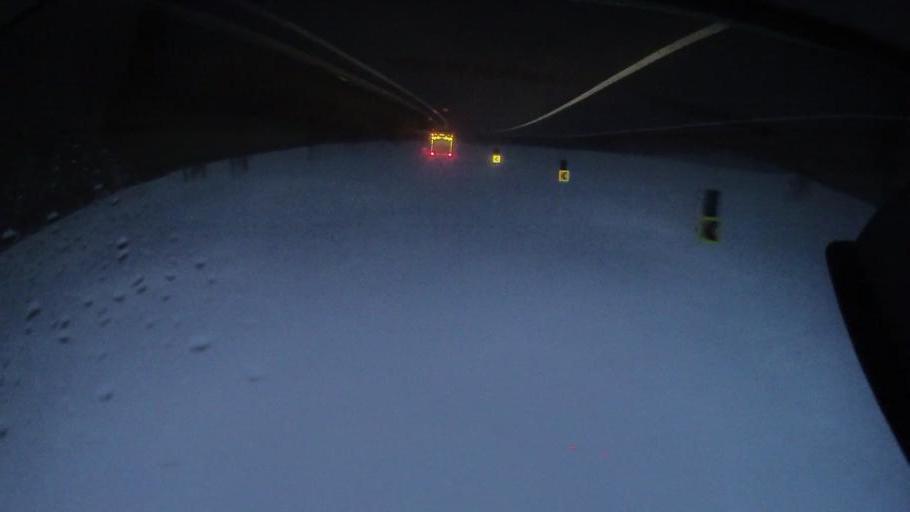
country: RO
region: Harghita
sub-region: Comuna Subcetate
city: Subcetate
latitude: 46.8464
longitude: 25.4698
